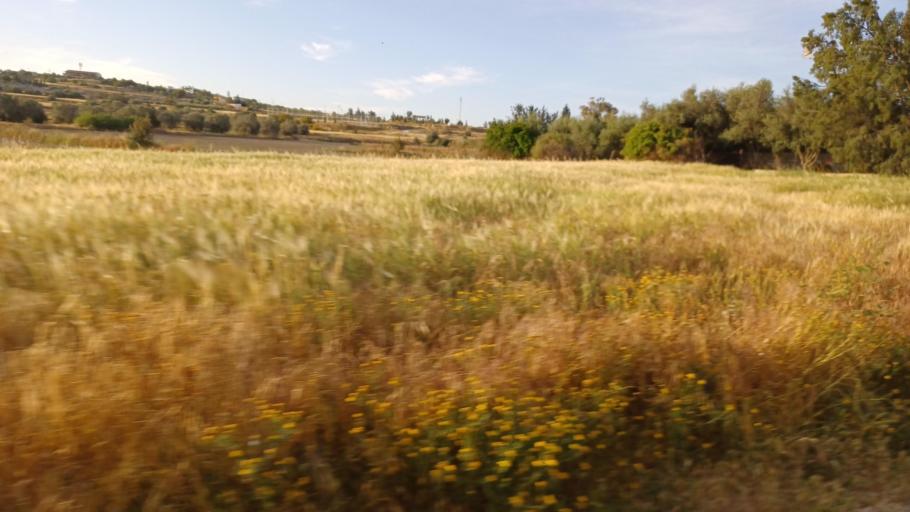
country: CY
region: Lefkosia
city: Akaki
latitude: 35.1691
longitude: 33.1498
